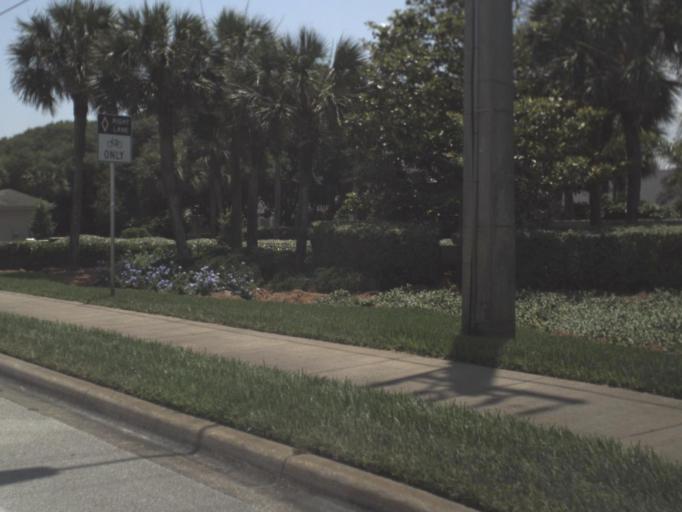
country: US
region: Florida
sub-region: Saint Johns County
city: Butler Beach
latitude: 29.8114
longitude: -81.2674
